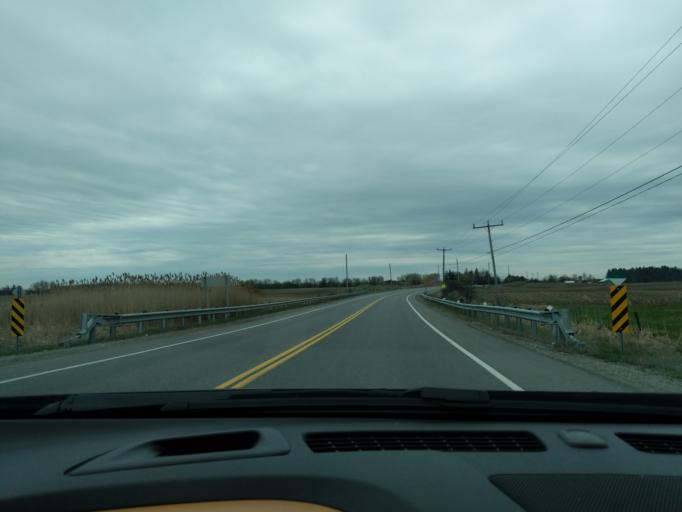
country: CA
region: Ontario
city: Brampton
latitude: 43.8289
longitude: -79.8158
